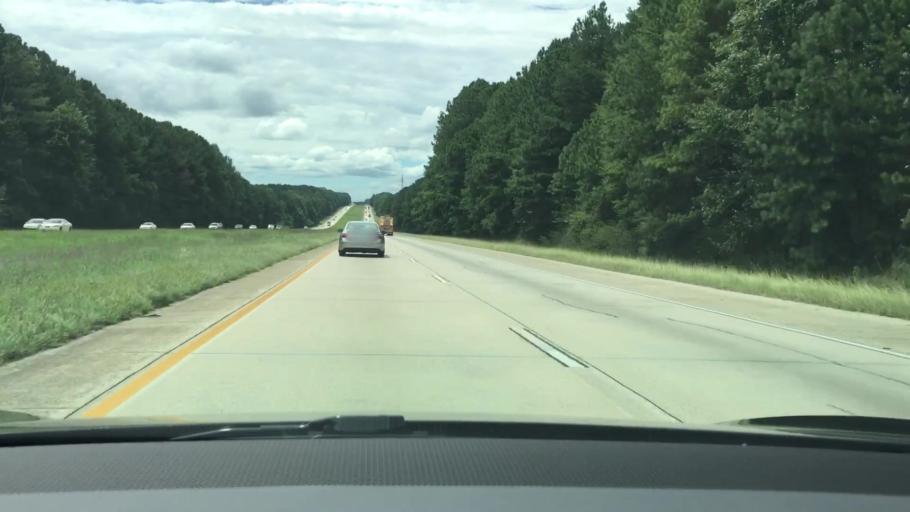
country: US
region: Georgia
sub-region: Coweta County
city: Grantville
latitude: 33.2073
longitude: -84.8309
